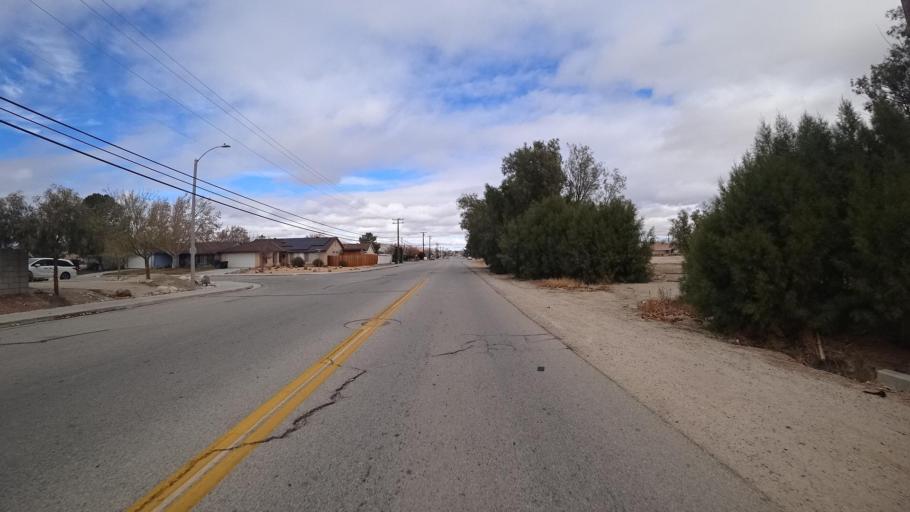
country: US
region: California
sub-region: Kern County
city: Rosamond
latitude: 34.8551
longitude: -118.1671
